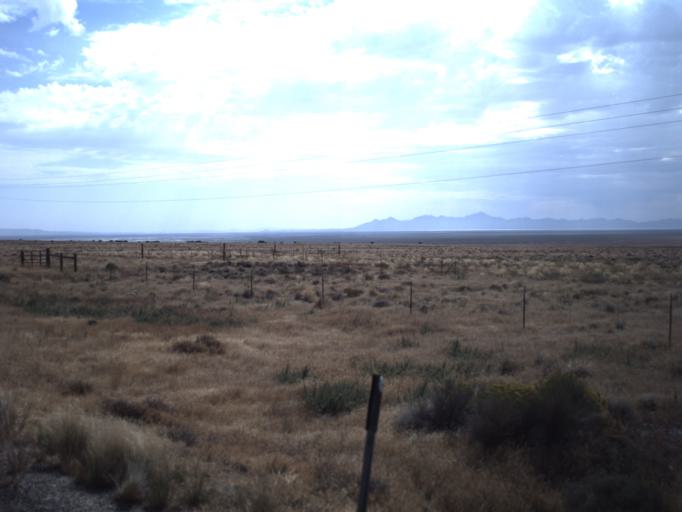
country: US
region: Utah
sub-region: Tooele County
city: Wendover
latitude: 41.4331
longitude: -113.7784
